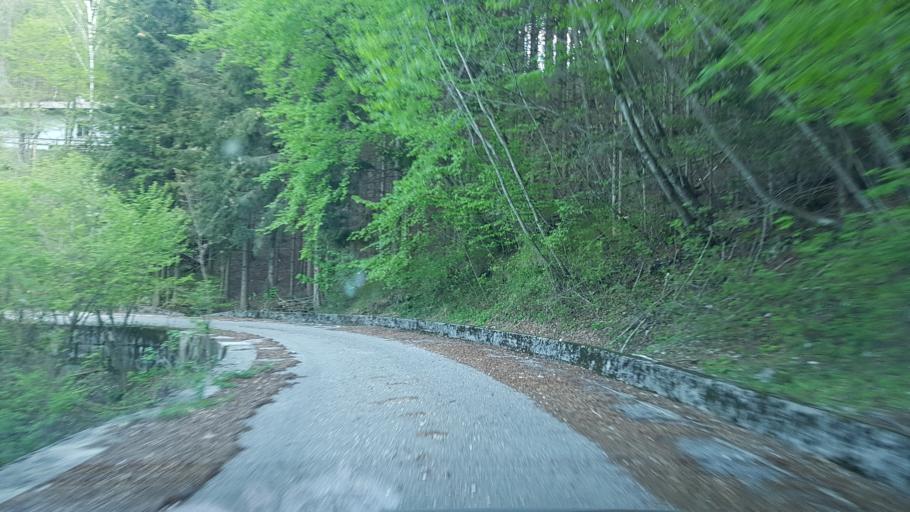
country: IT
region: Friuli Venezia Giulia
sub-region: Provincia di Udine
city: Cavazzo Carnico
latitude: 46.3123
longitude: 13.0236
